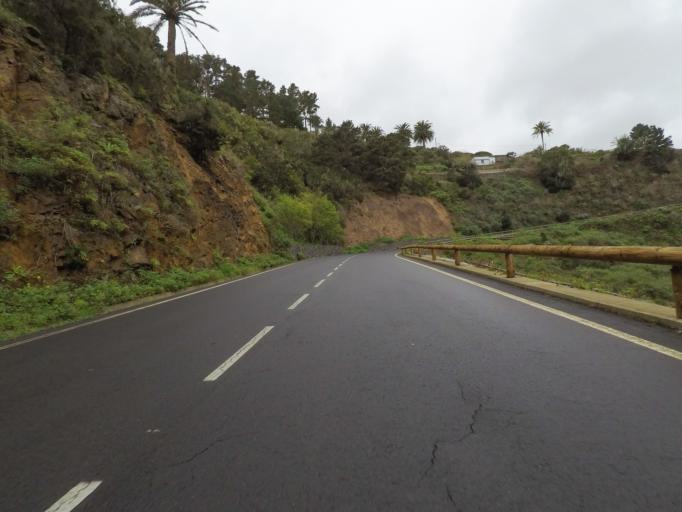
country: ES
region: Canary Islands
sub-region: Provincia de Santa Cruz de Tenerife
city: Agulo
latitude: 28.1866
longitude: -17.2178
